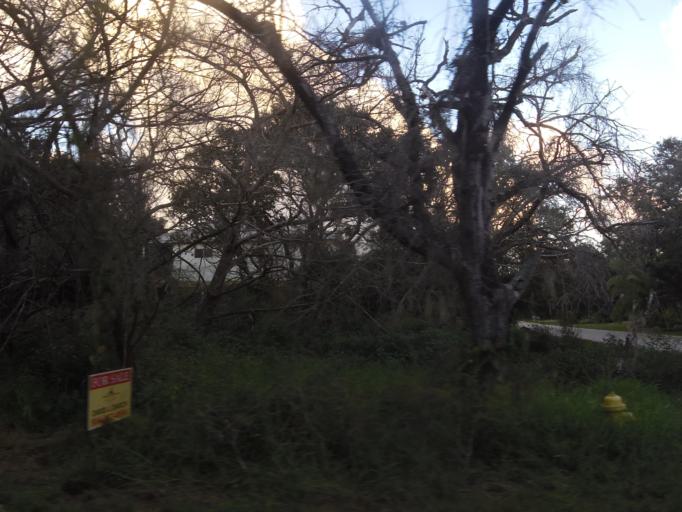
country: US
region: Florida
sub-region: Saint Johns County
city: Villano Beach
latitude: 29.9533
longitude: -81.3106
